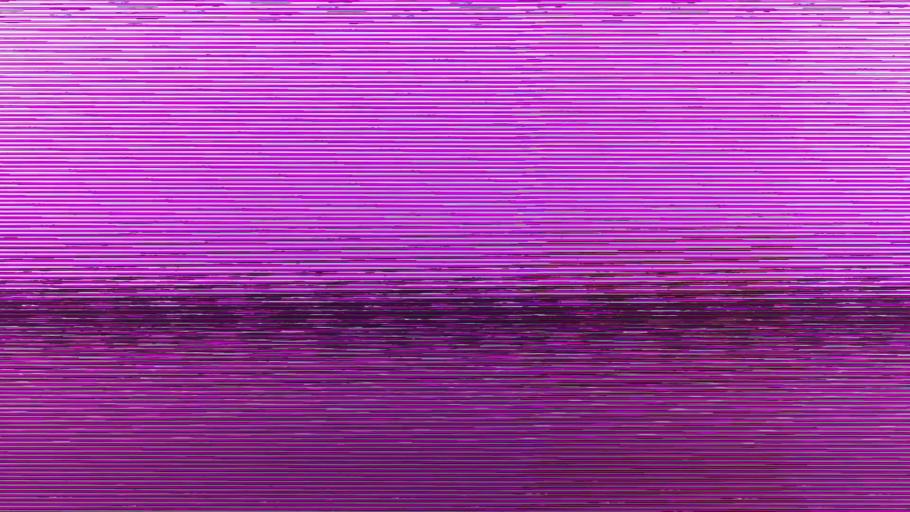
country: US
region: Michigan
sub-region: Wayne County
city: Belleville
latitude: 42.2217
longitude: -83.4852
